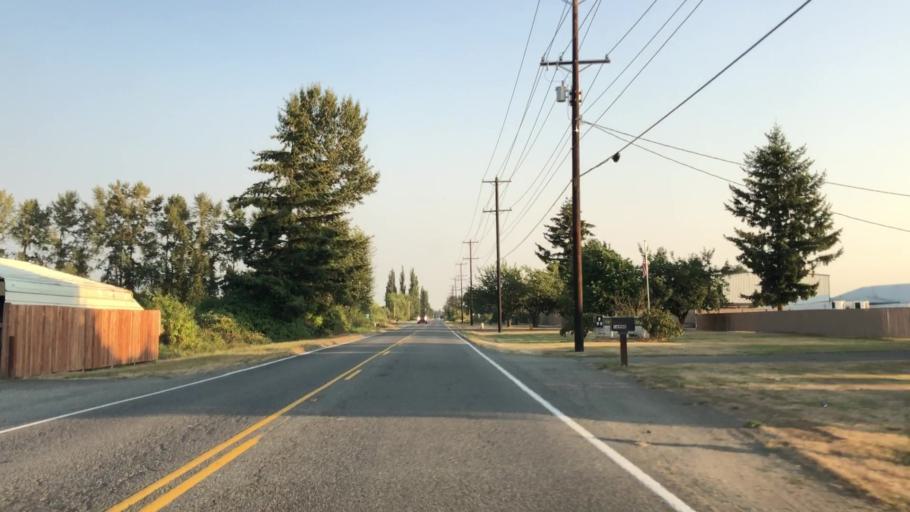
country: US
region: Washington
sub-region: Snohomish County
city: Smokey Point
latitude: 48.1504
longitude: -122.1616
